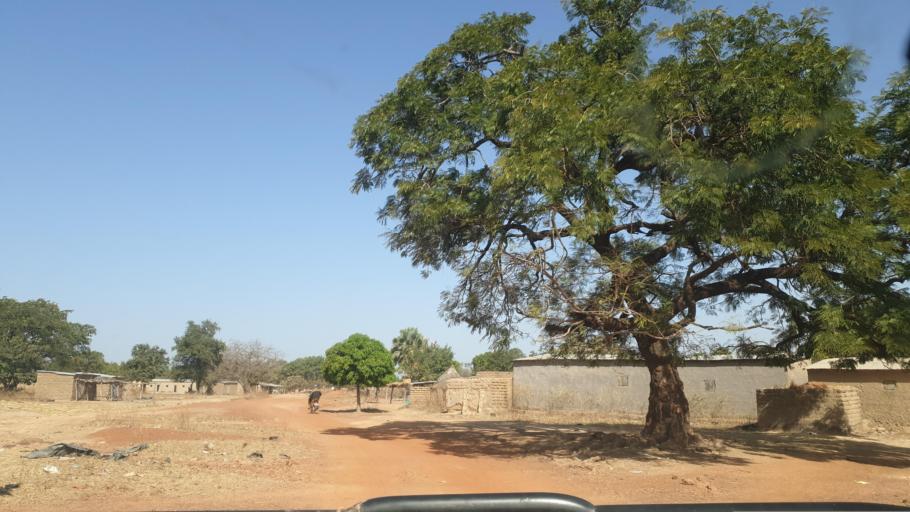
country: ML
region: Sikasso
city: Bougouni
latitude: 11.8136
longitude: -6.9355
